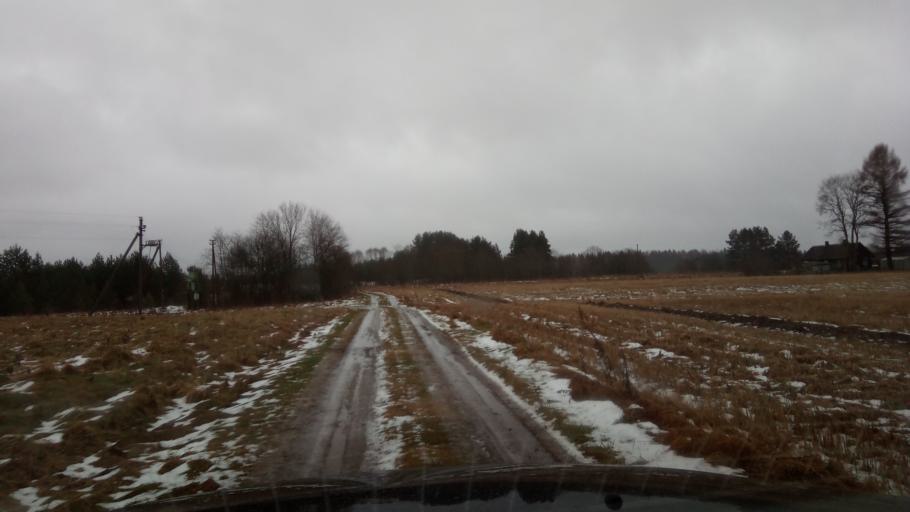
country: LT
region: Utenos apskritis
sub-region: Utena
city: Utena
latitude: 55.3695
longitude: 25.7626
